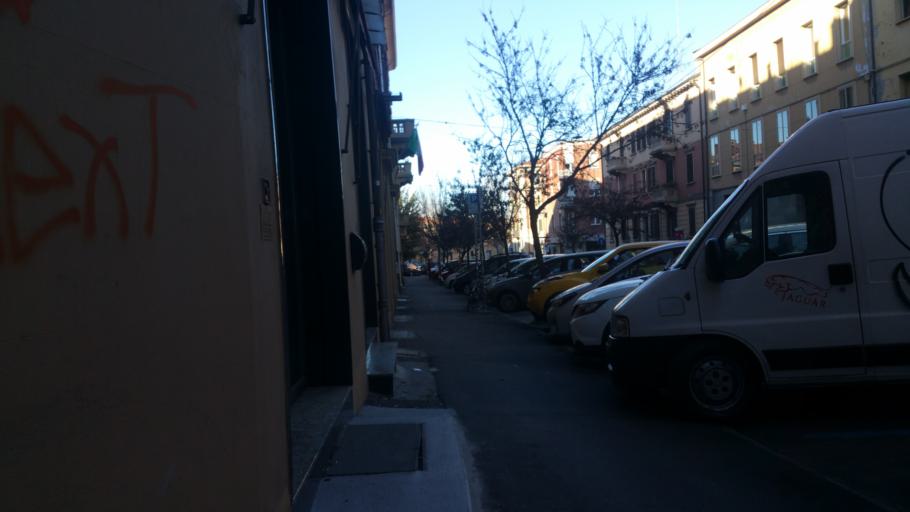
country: IT
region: Emilia-Romagna
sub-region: Provincia di Bologna
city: Bologna
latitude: 44.5006
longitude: 11.3242
